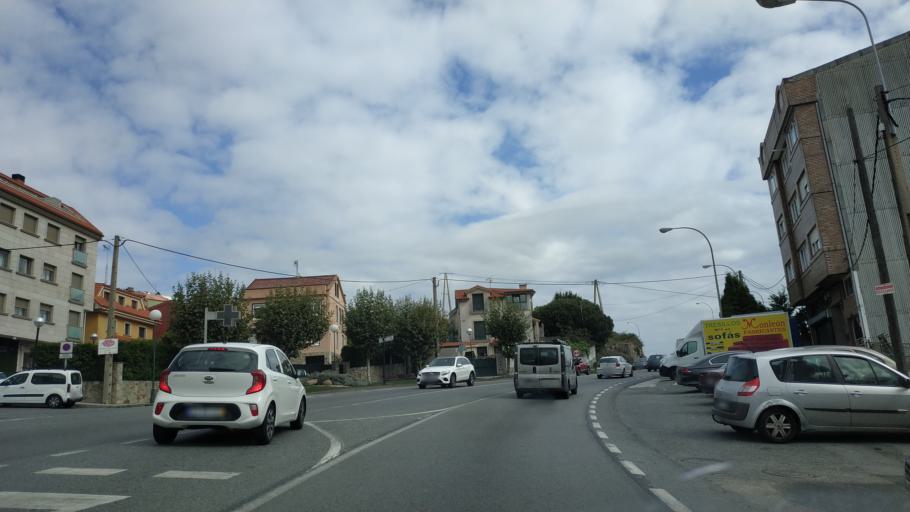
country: ES
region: Galicia
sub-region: Provincia da Coruna
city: Arteixo
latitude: 43.3293
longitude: -8.4654
